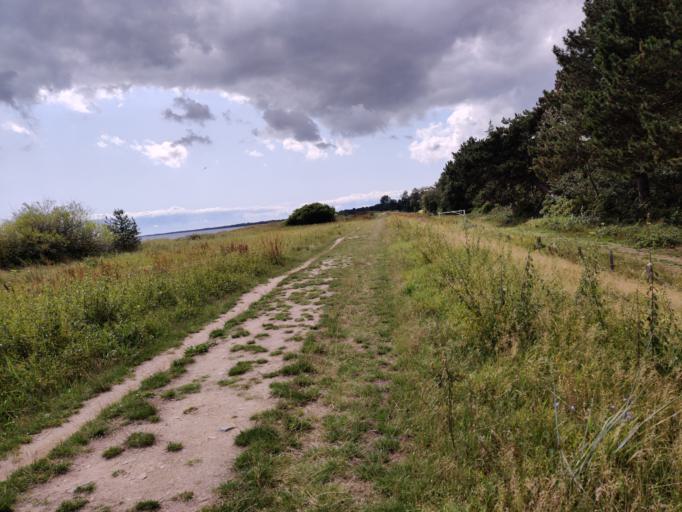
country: DK
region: Zealand
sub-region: Guldborgsund Kommune
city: Nykobing Falster
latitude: 54.7117
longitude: 11.9923
